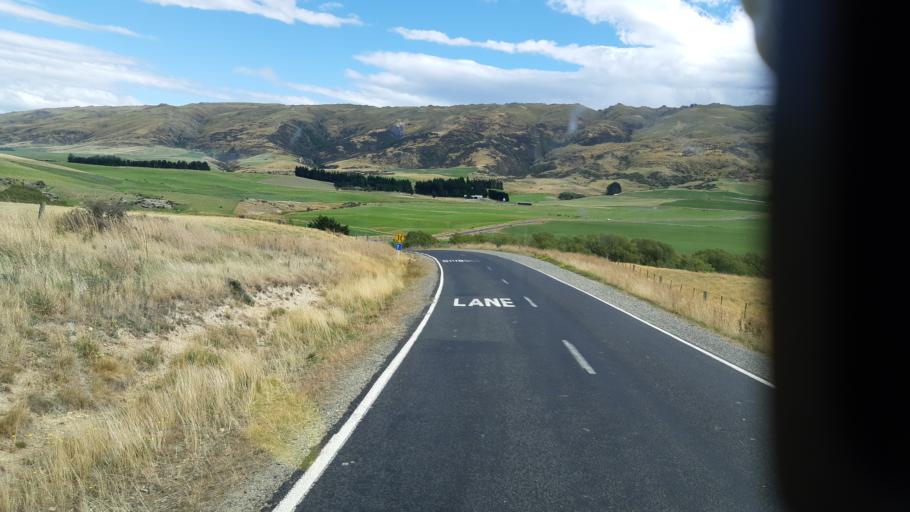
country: NZ
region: Otago
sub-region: Dunedin City
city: Dunedin
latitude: -45.3181
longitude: 170.2657
